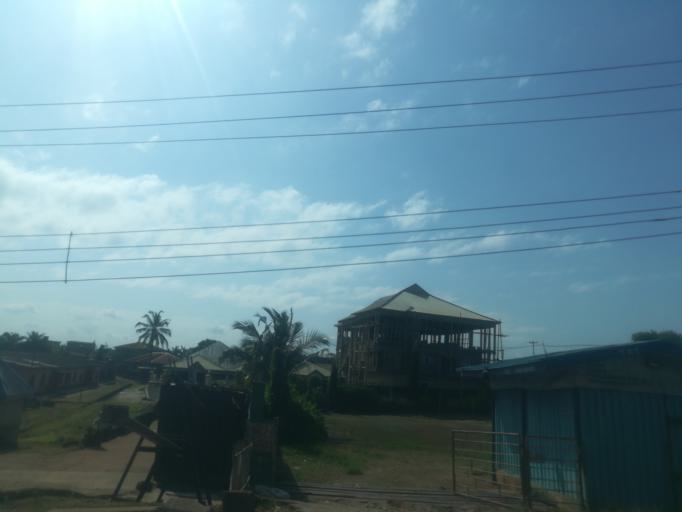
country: NG
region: Oyo
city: Ibadan
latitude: 7.4166
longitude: 3.9629
